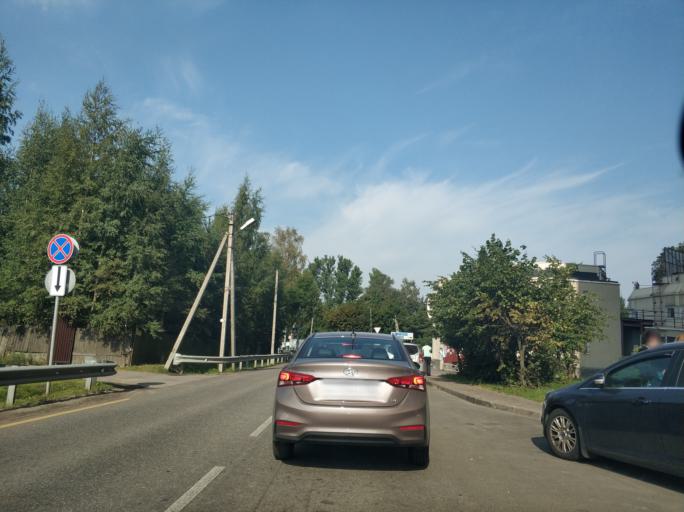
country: RU
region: Leningrad
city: Murino
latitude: 60.0464
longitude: 30.4616
